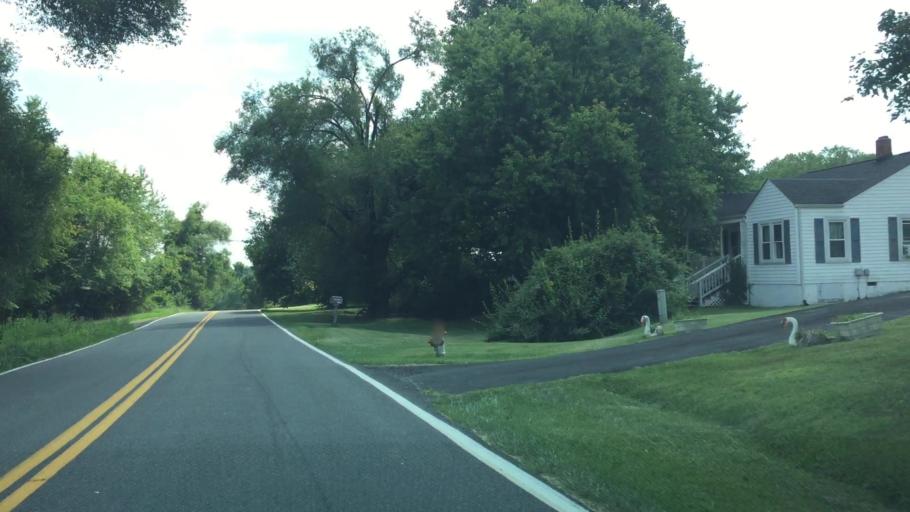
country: US
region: Virginia
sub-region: Pulaski County
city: Pulaski
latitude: 37.0024
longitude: -80.7995
